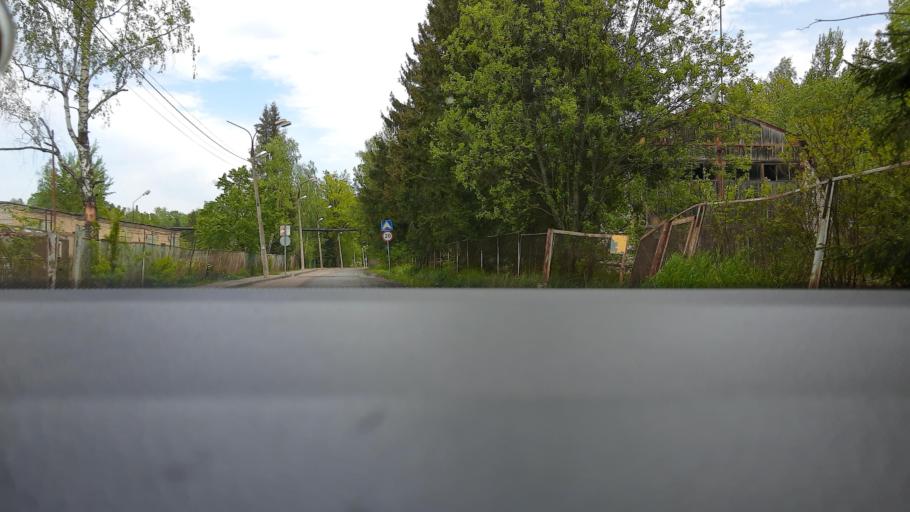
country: RU
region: Moskovskaya
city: Povedniki
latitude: 55.9452
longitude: 37.6617
